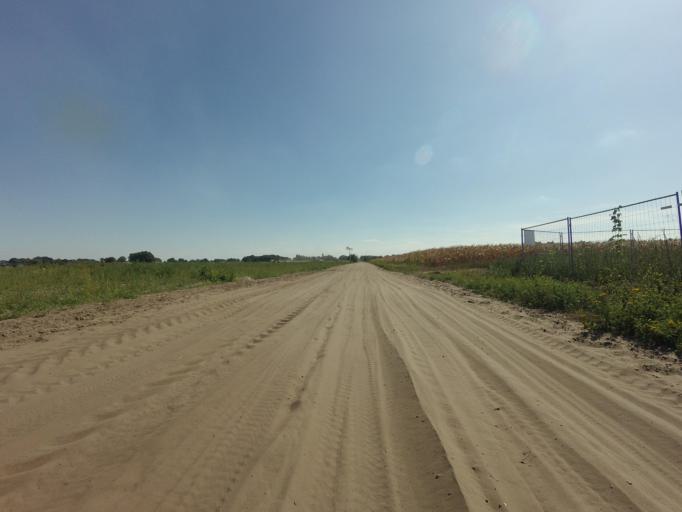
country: NL
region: North Brabant
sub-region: Gemeente Someren
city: Someren
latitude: 51.3841
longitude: 5.6688
